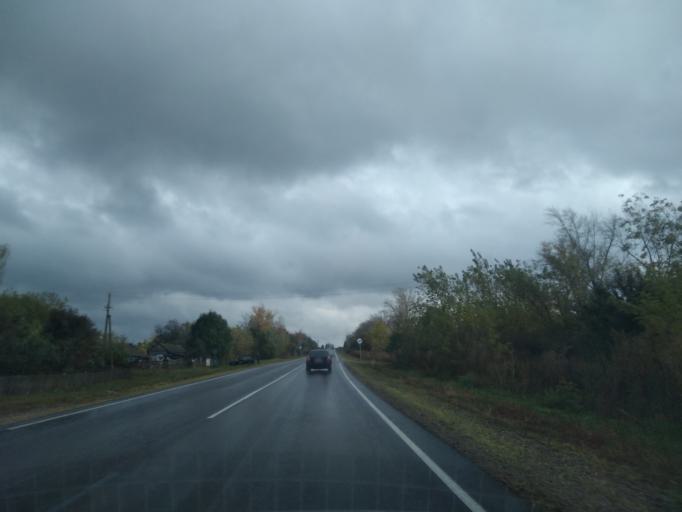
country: RU
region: Tula
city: Kazachka
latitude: 53.3670
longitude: 37.8576
